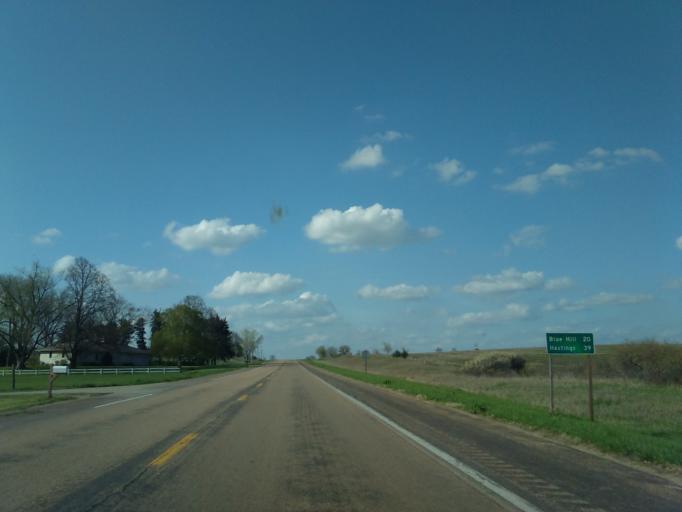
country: US
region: Nebraska
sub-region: Webster County
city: Red Cloud
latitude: 40.1036
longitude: -98.5188
